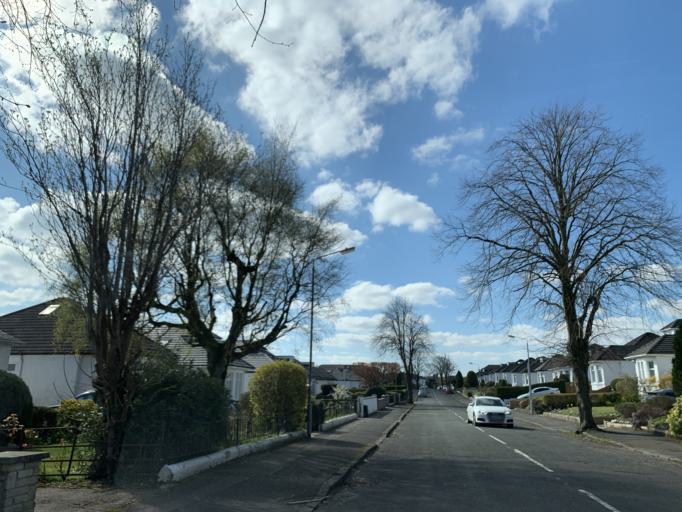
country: GB
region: Scotland
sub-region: East Renfrewshire
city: Clarkston
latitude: 55.7926
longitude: -4.2722
